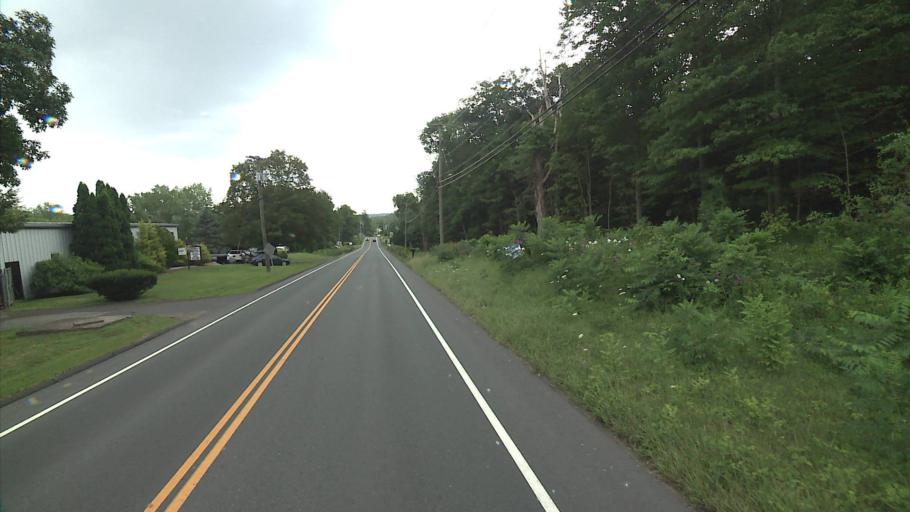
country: US
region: Connecticut
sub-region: New Haven County
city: Southbury
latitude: 41.4659
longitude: -73.1674
